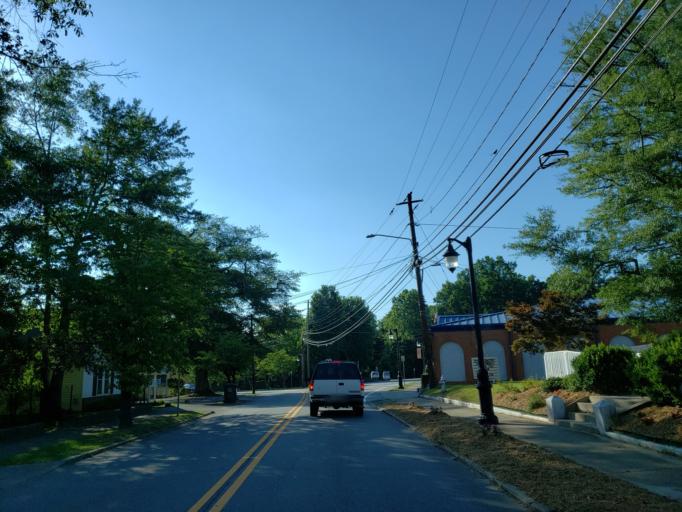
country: US
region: Georgia
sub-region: Cherokee County
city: Canton
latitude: 34.2361
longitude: -84.4872
